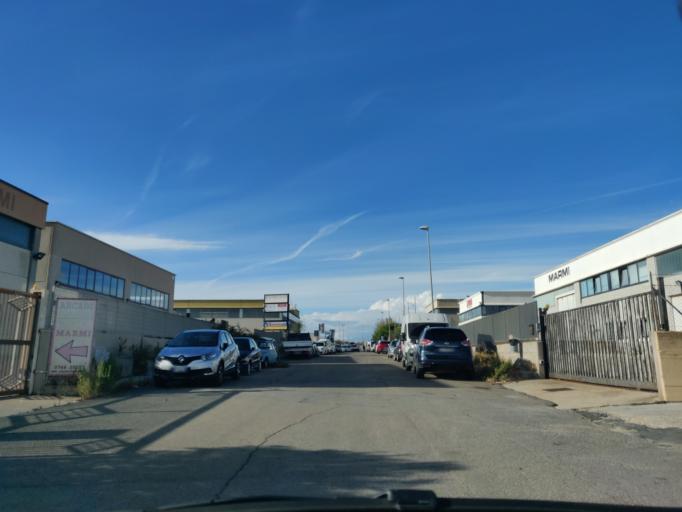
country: IT
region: Latium
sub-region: Citta metropolitana di Roma Capitale
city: Aurelia
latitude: 42.1184
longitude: 11.7829
